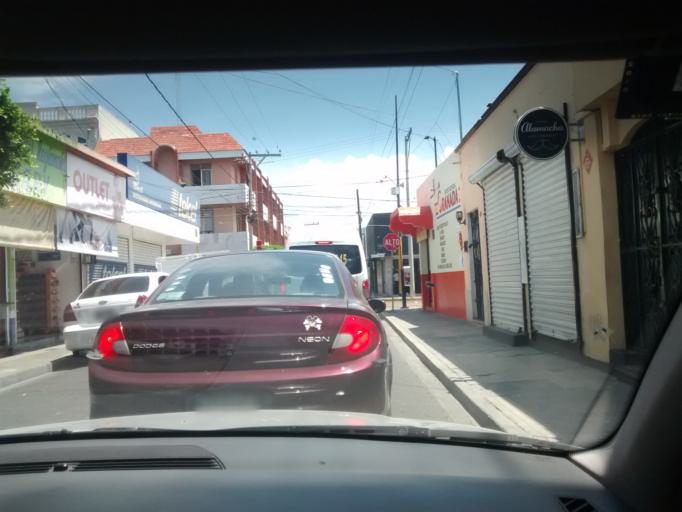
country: MX
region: Puebla
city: Tehuacan
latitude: 18.4621
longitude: -97.3961
